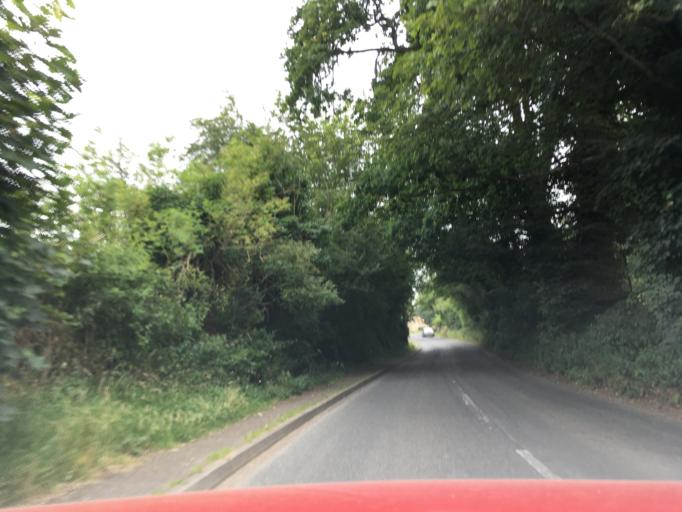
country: GB
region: England
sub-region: Oxfordshire
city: Charlbury
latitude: 51.9214
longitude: -1.4521
